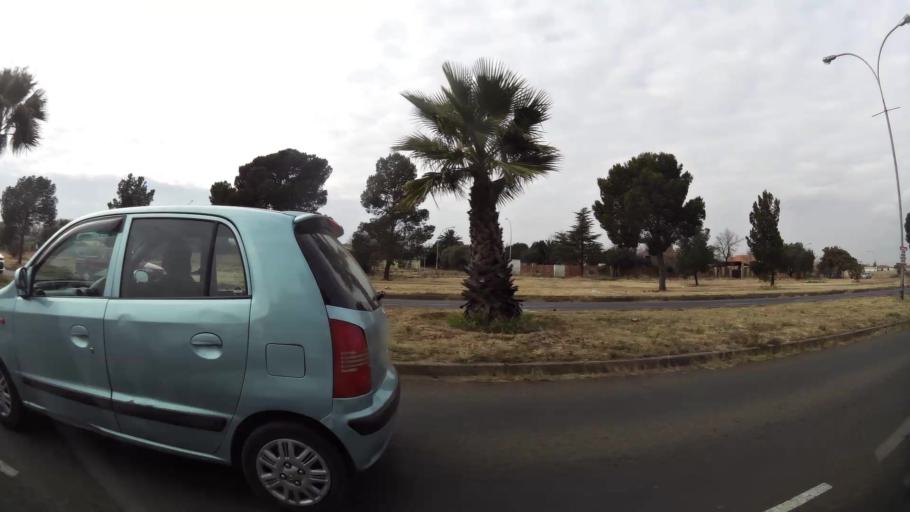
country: ZA
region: Orange Free State
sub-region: Mangaung Metropolitan Municipality
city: Bloemfontein
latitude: -29.1517
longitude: 26.1902
